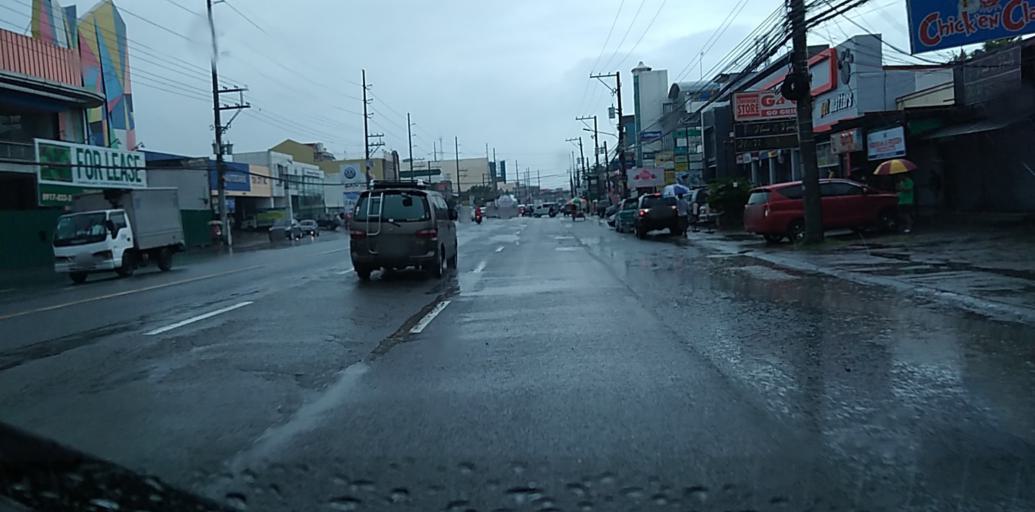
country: PH
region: Central Luzon
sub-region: Province of Pampanga
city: Magliman
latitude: 15.0413
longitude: 120.6776
